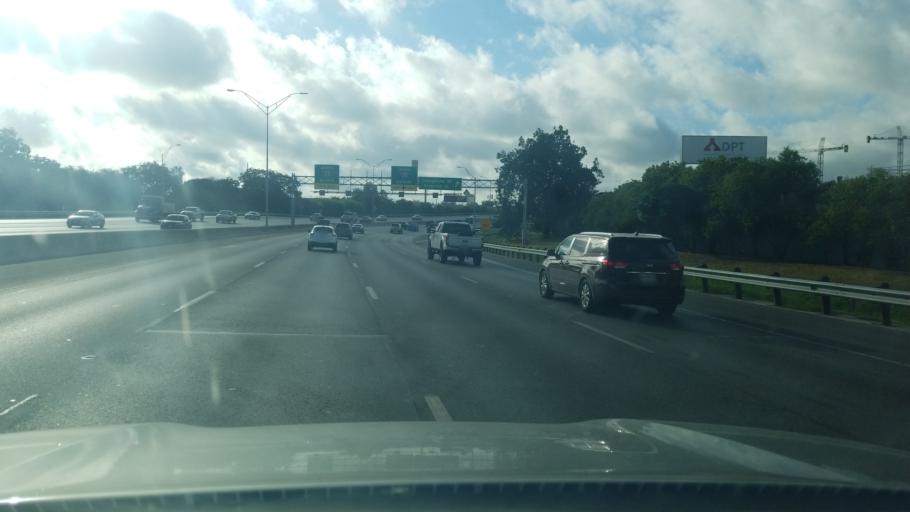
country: US
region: Texas
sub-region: Bexar County
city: San Antonio
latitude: 29.4471
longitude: -98.4802
